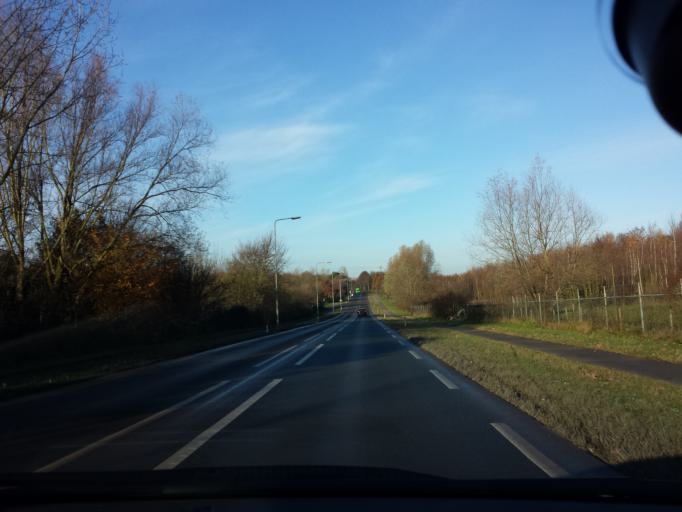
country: NL
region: Limburg
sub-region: Gemeente Brunssum
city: Brunssum
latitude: 50.9291
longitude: 6.0256
